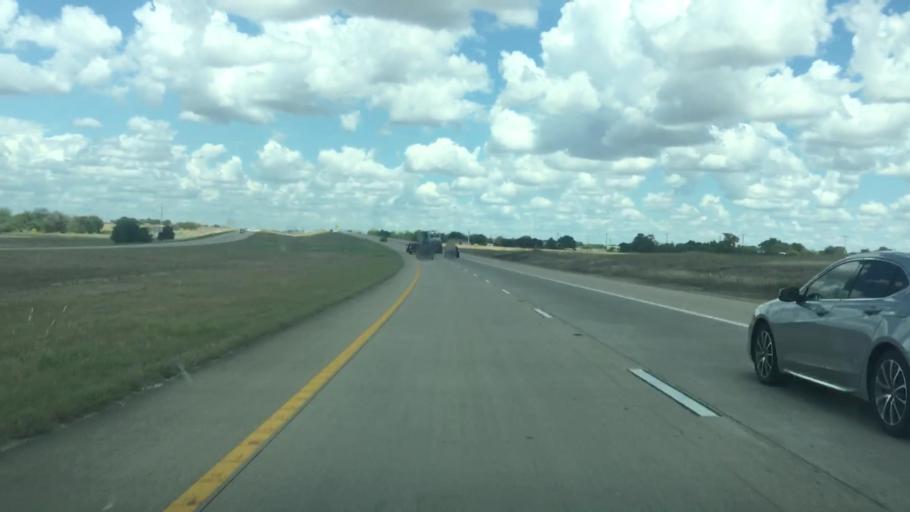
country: US
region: Texas
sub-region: Williamson County
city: Hutto
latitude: 30.5563
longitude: -97.5769
